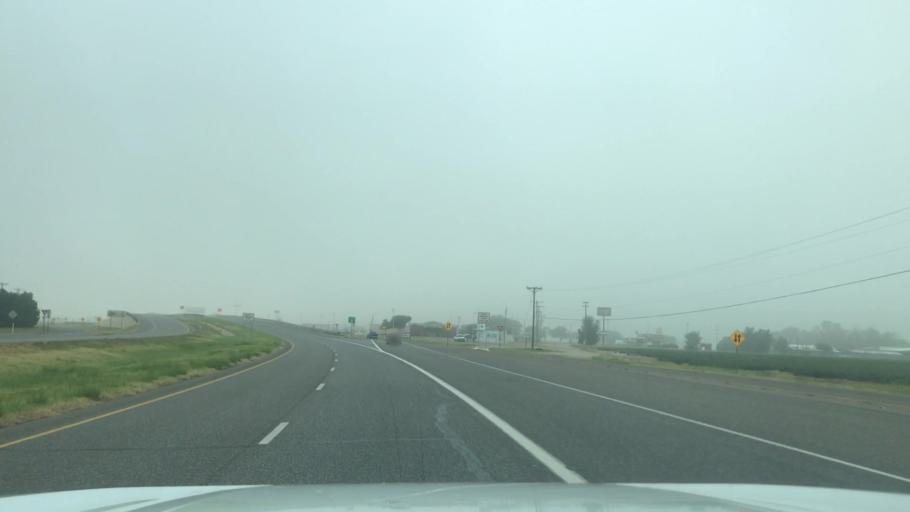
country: US
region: Texas
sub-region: Lubbock County
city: Slaton
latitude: 33.4376
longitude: -101.6660
